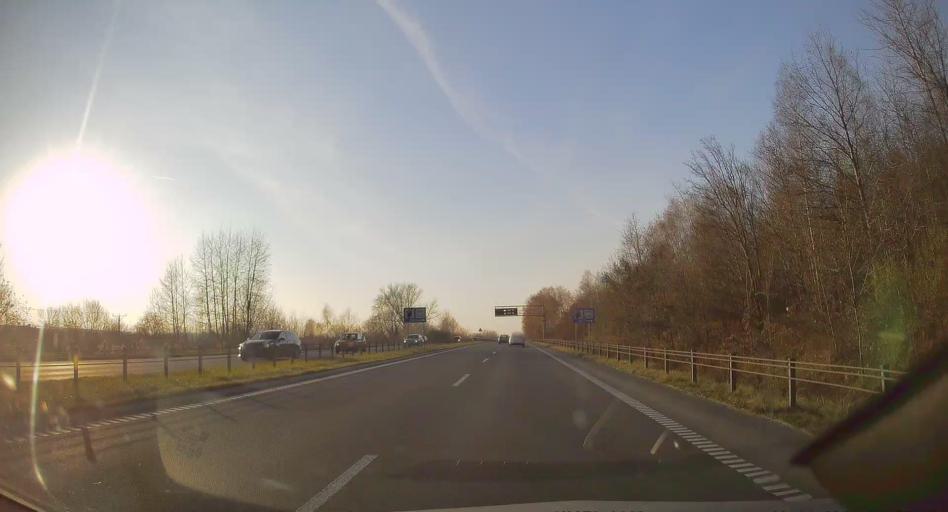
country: PL
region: Silesian Voivodeship
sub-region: Dabrowa Gornicza
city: Dabrowa Gornicza
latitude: 50.3172
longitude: 19.2607
